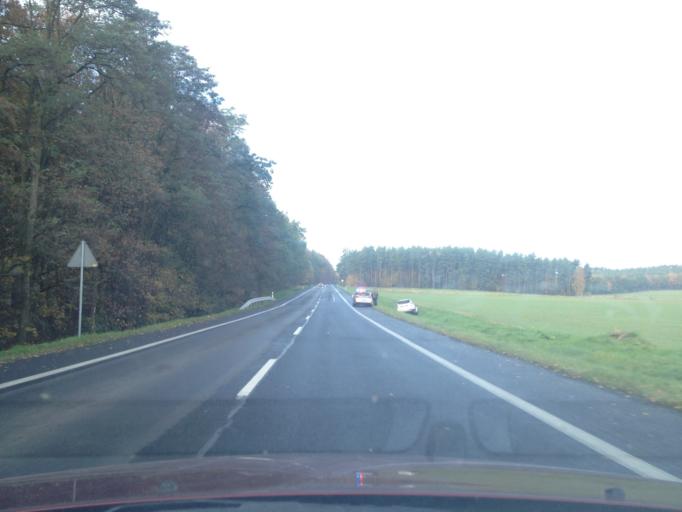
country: PL
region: Lower Silesian Voivodeship
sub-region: Powiat lubanski
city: Siekierczyn
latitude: 51.1536
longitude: 15.1584
